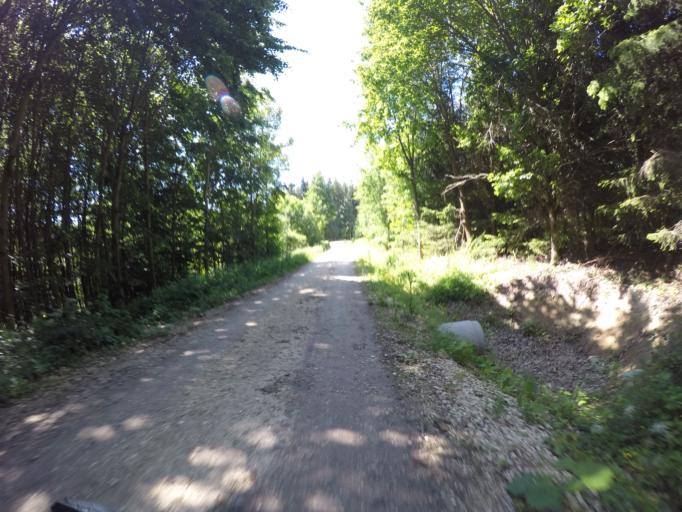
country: DE
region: Bavaria
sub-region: Lower Bavaria
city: Kumhausen
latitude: 48.5054
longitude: 12.1942
